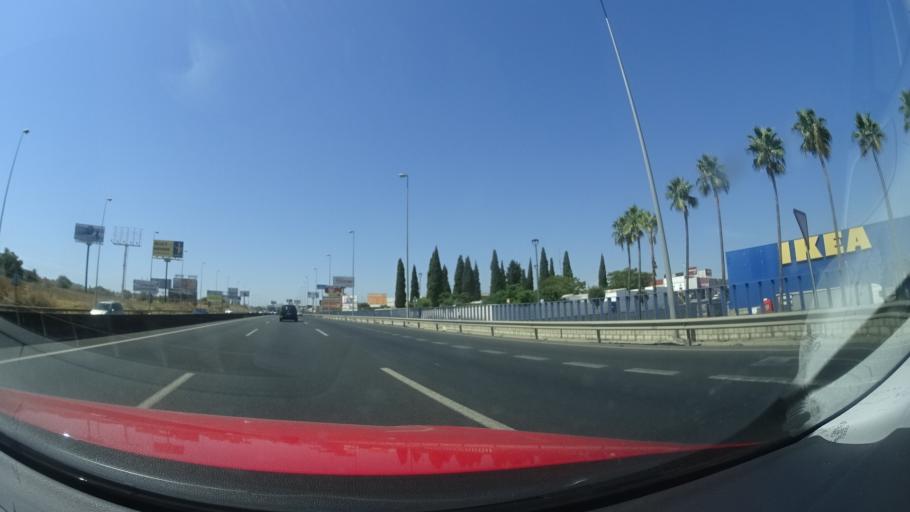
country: ES
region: Andalusia
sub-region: Provincia de Sevilla
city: Castilleja de la Cuesta
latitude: 37.3825
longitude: -6.0477
